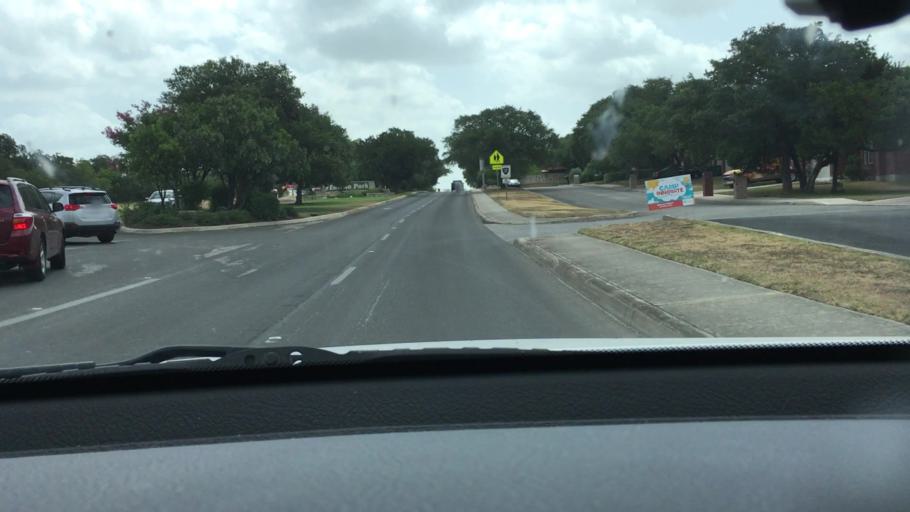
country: US
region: Texas
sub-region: Bexar County
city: Hollywood Park
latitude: 29.6301
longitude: -98.4571
